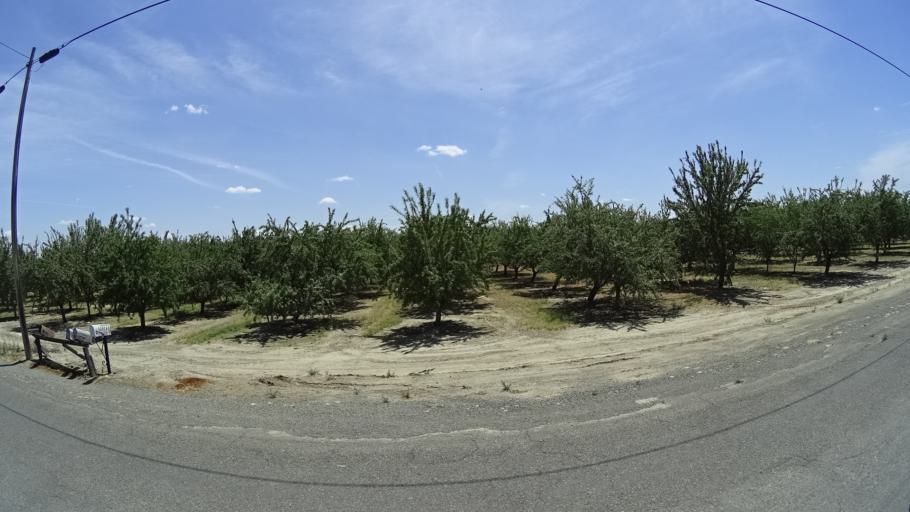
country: US
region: California
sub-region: Kings County
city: Armona
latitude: 36.2839
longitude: -119.7009
